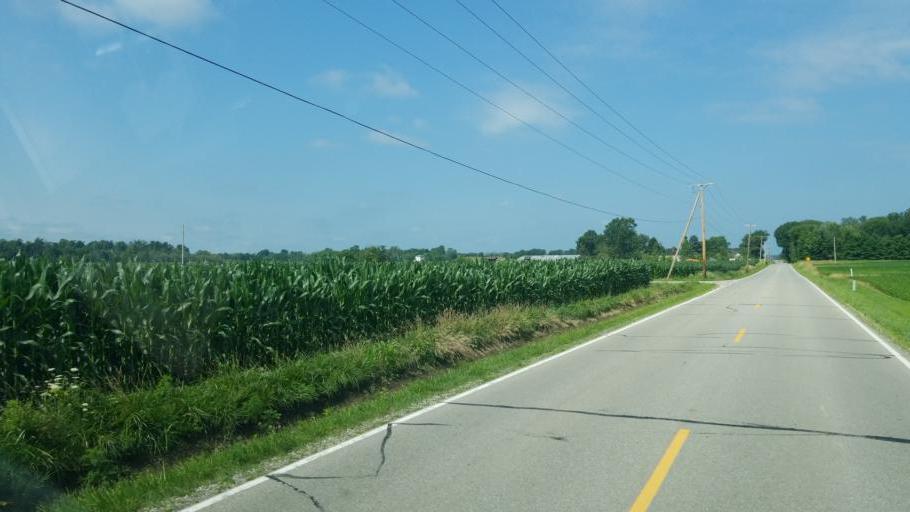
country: US
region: Ohio
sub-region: Crawford County
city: Galion
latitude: 40.7560
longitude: -82.8042
